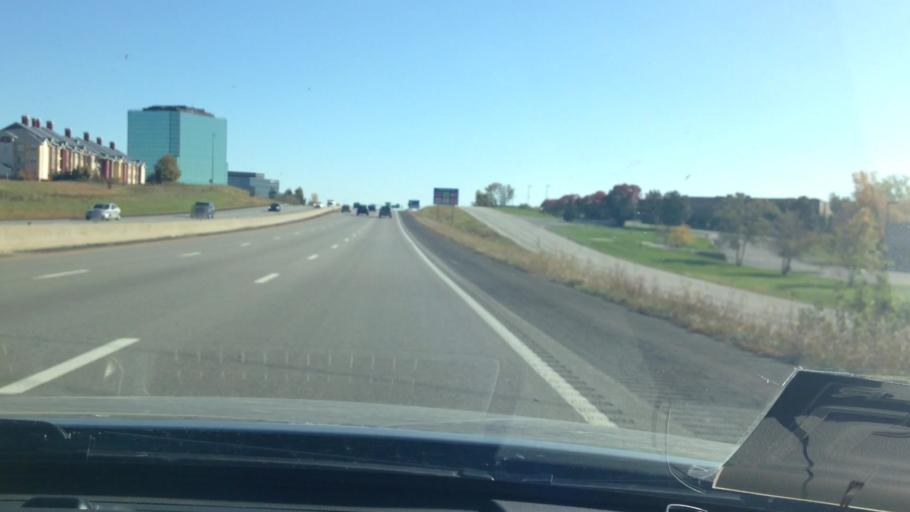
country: US
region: Missouri
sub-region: Platte County
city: Weatherby Lake
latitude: 39.2823
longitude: -94.6762
